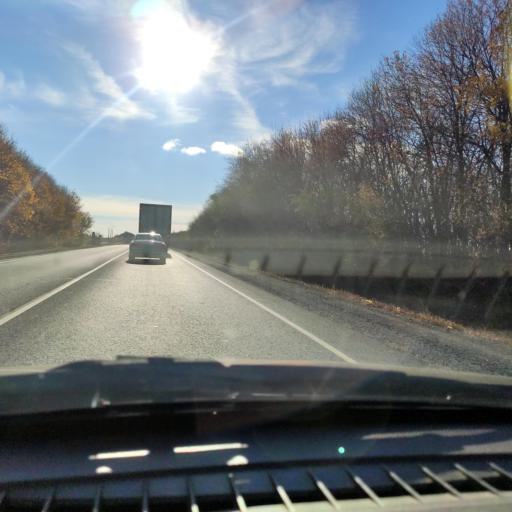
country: RU
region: Samara
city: Zhigulevsk
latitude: 53.3184
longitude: 49.3665
